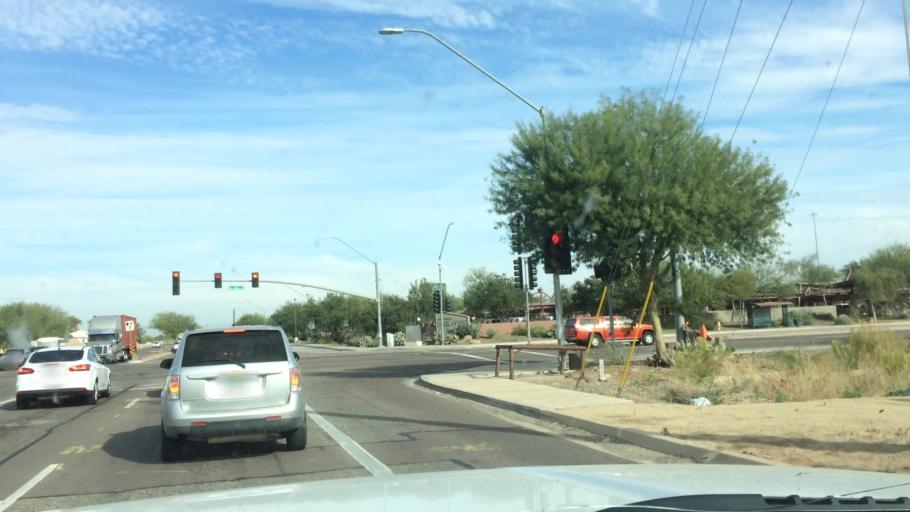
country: US
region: Arizona
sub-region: Maricopa County
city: Peoria
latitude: 33.5367
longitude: -112.2724
